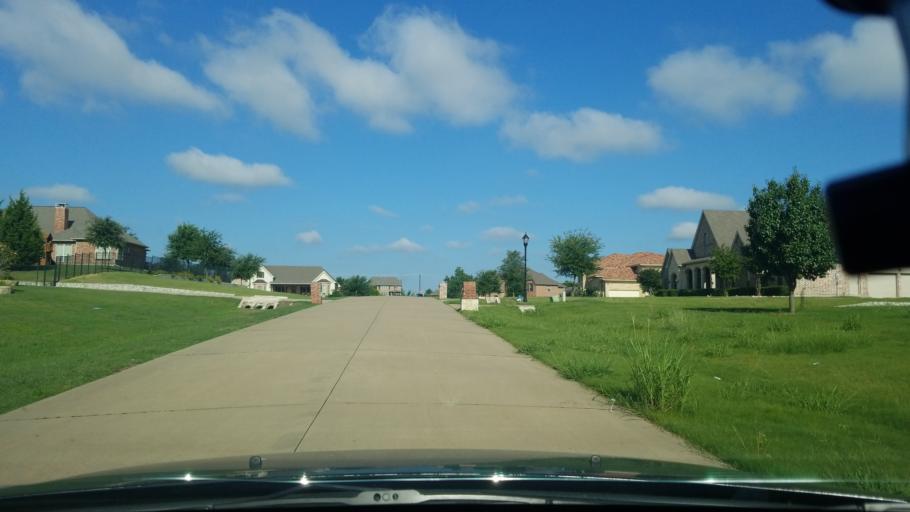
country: US
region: Texas
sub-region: Dallas County
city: Sunnyvale
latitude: 32.8090
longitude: -96.5580
